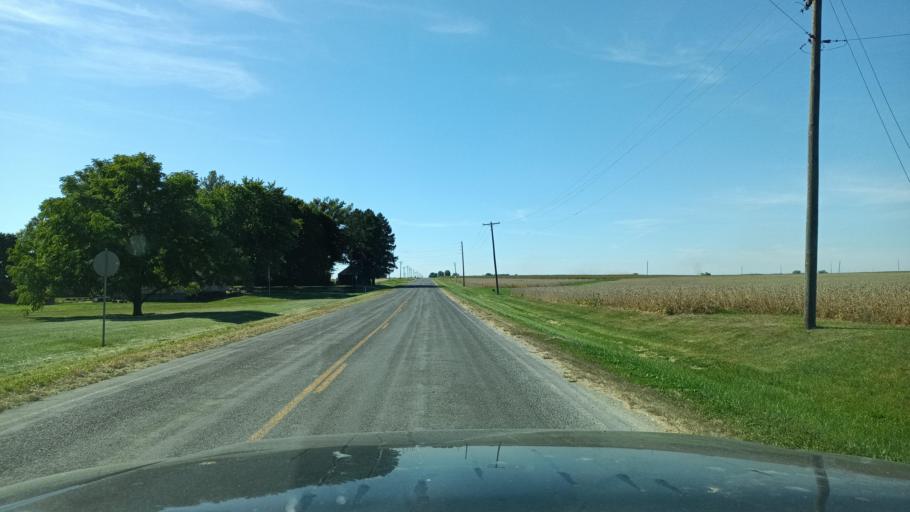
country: US
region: Illinois
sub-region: De Witt County
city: Farmer City
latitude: 40.2239
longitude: -88.7185
